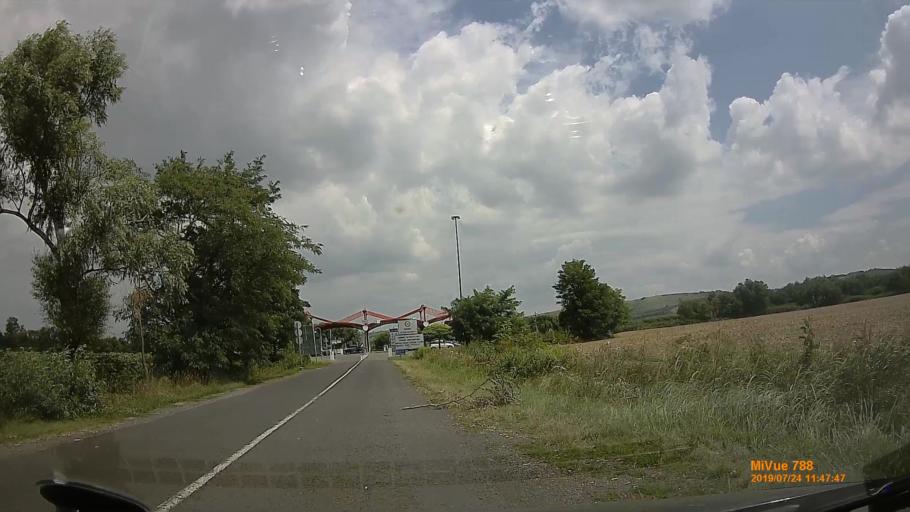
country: UA
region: Zakarpattia
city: Batiovo
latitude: 48.2446
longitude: 22.4441
